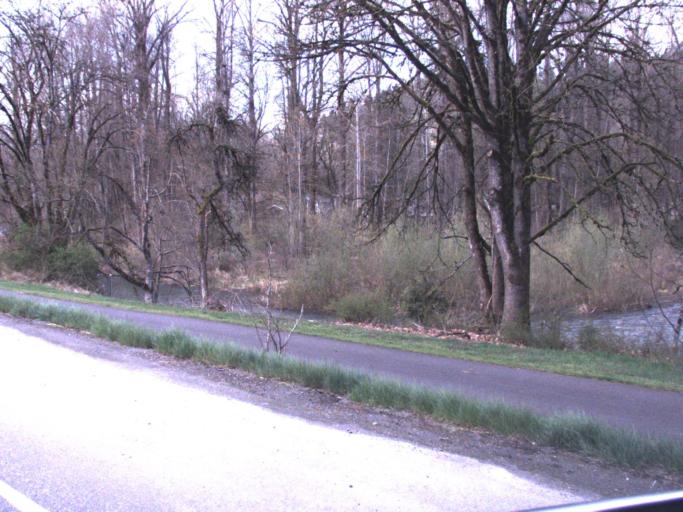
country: US
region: Washington
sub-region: King County
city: East Renton Highlands
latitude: 47.4632
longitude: -122.1191
